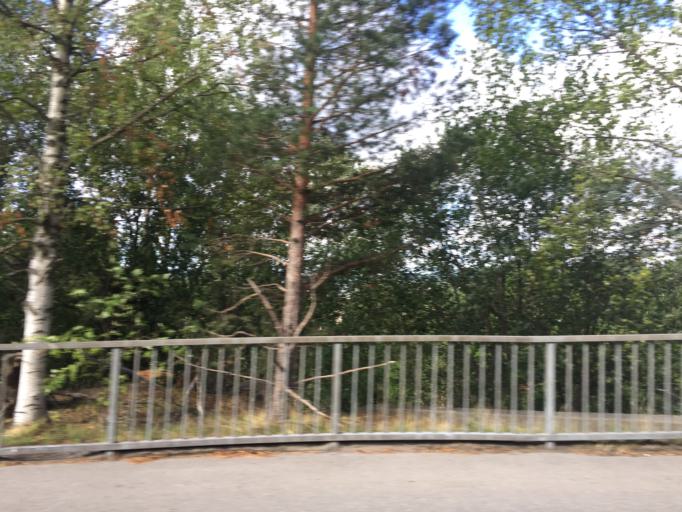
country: NO
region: Akershus
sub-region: Skedsmo
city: Lillestrom
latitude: 59.9307
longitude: 11.0338
